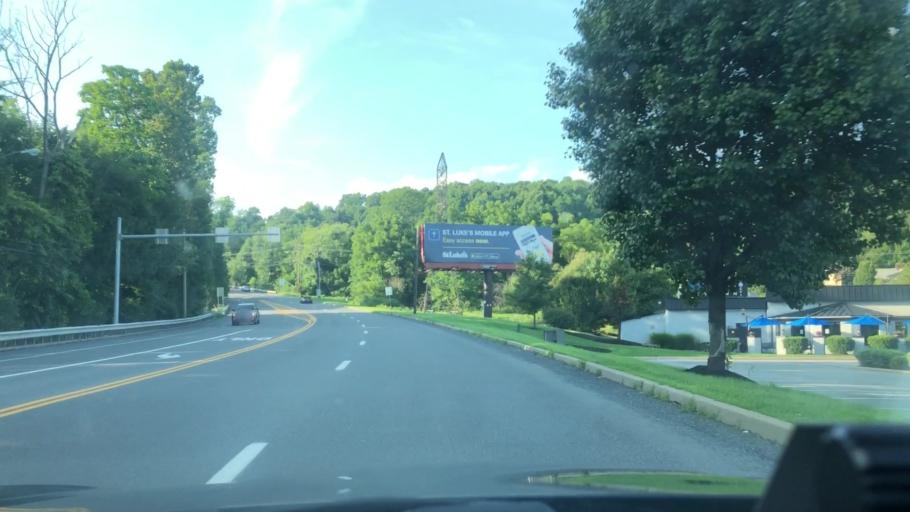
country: US
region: Pennsylvania
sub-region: Lehigh County
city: Fountain Hill
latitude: 40.5869
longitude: -75.3864
